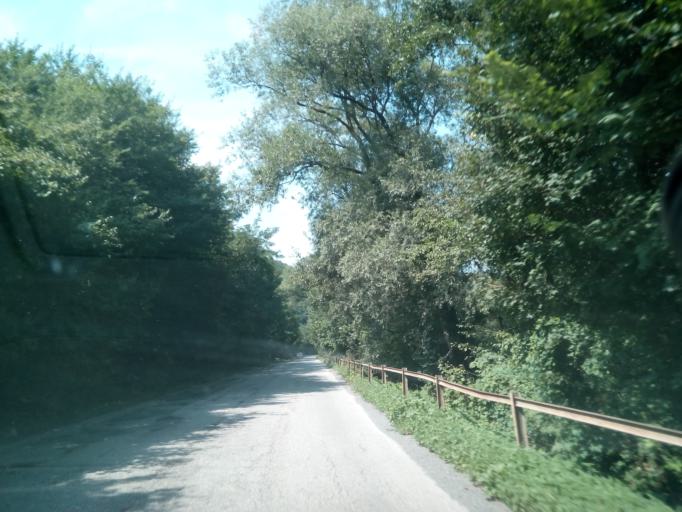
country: SK
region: Presovsky
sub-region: Okres Presov
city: Presov
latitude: 48.8619
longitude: 21.2160
